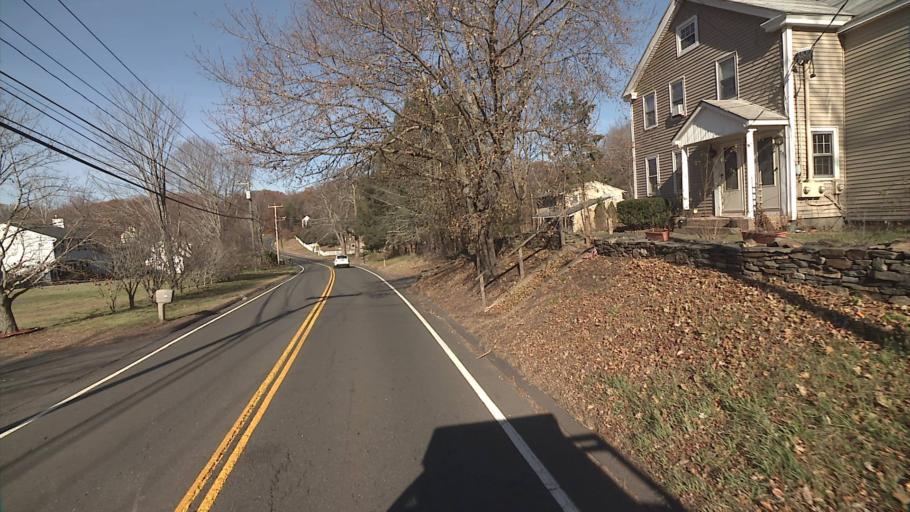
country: US
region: Connecticut
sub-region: Middlesex County
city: Cromwell
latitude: 41.6251
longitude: -72.6014
